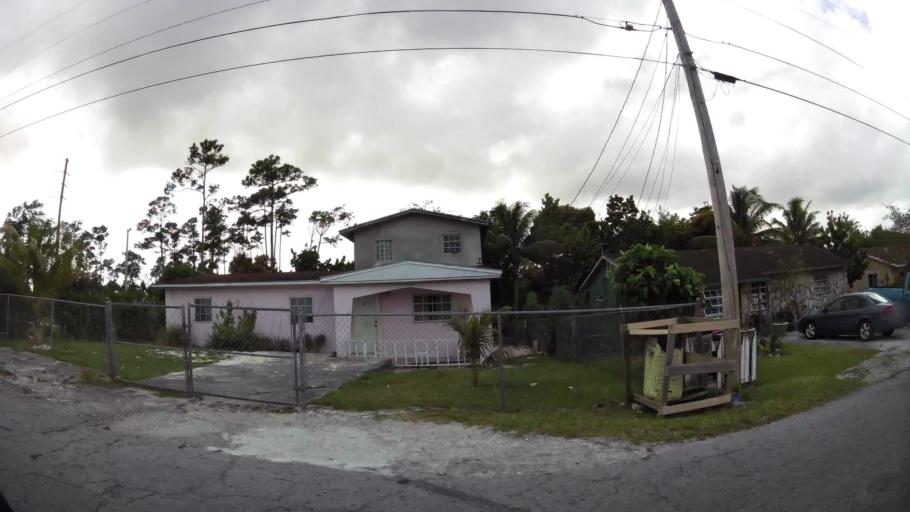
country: BS
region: Freeport
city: Freeport
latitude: 26.5303
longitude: -78.7021
